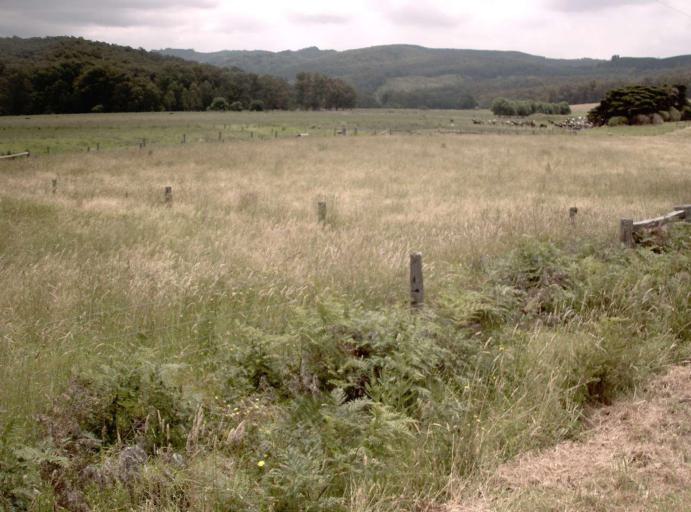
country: AU
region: Victoria
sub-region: Latrobe
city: Traralgon
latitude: -38.4812
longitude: 146.6817
